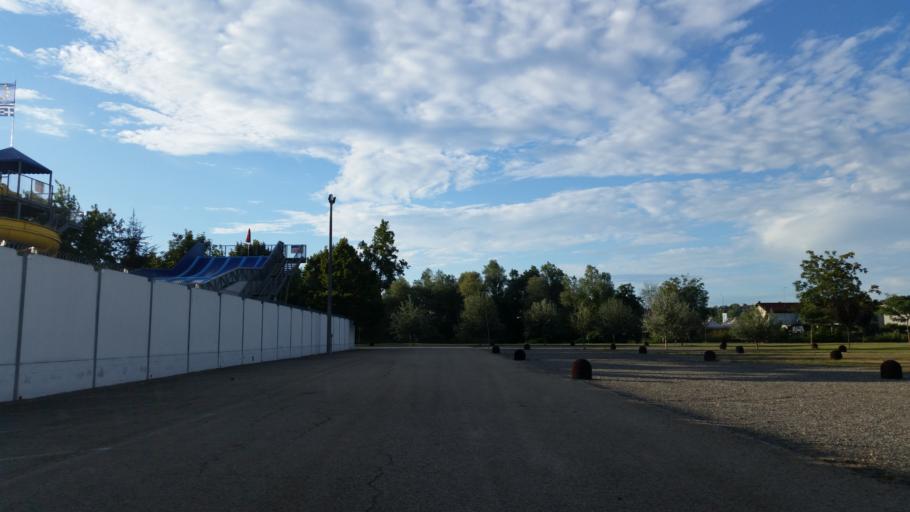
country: IT
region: Piedmont
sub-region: Provincia di Asti
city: Asti
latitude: 44.9028
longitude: 8.1778
